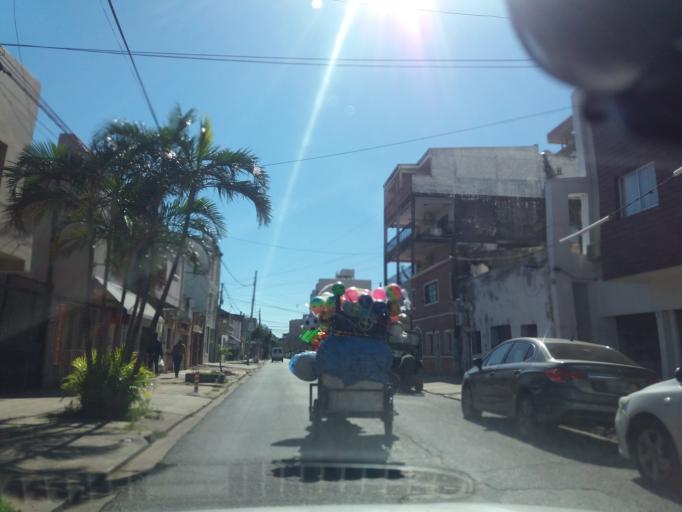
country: AR
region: Corrientes
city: Corrientes
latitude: -27.4736
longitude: -58.8435
